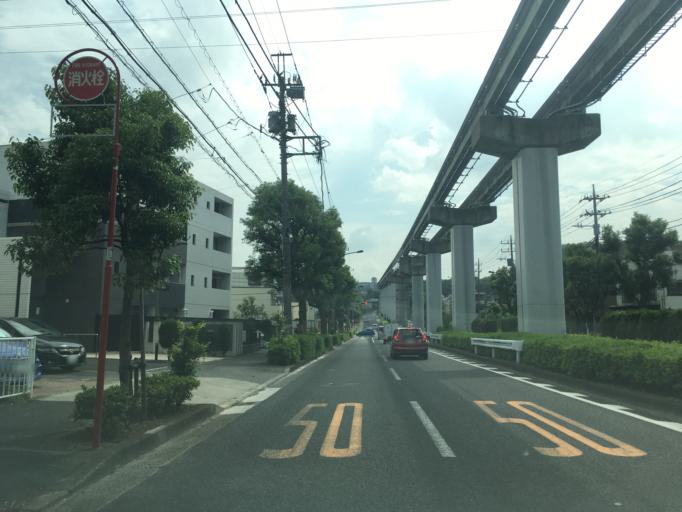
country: JP
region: Tokyo
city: Hino
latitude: 35.6361
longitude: 139.4177
